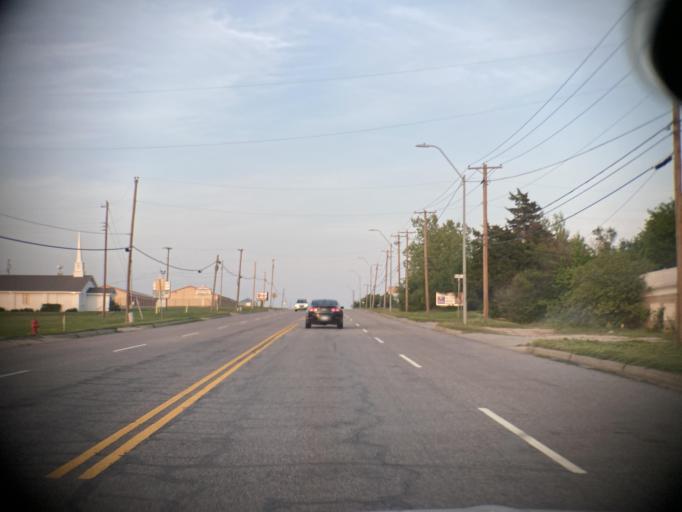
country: US
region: Oklahoma
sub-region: Oklahoma County
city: Midwest City
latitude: 35.4352
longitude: -97.3592
